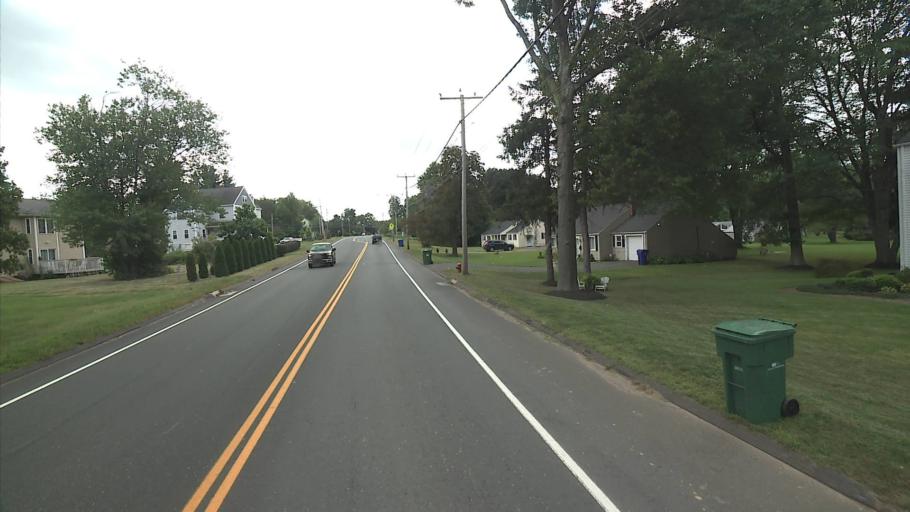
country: US
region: Connecticut
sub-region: Hartford County
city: Blue Hills
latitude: 41.8264
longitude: -72.7374
